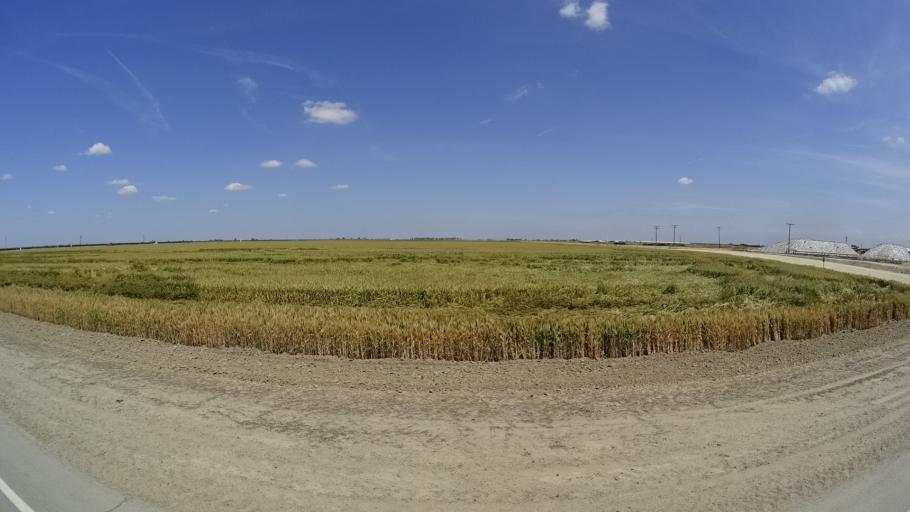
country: US
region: California
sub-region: Kings County
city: Home Garden
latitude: 36.2991
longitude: -119.5301
